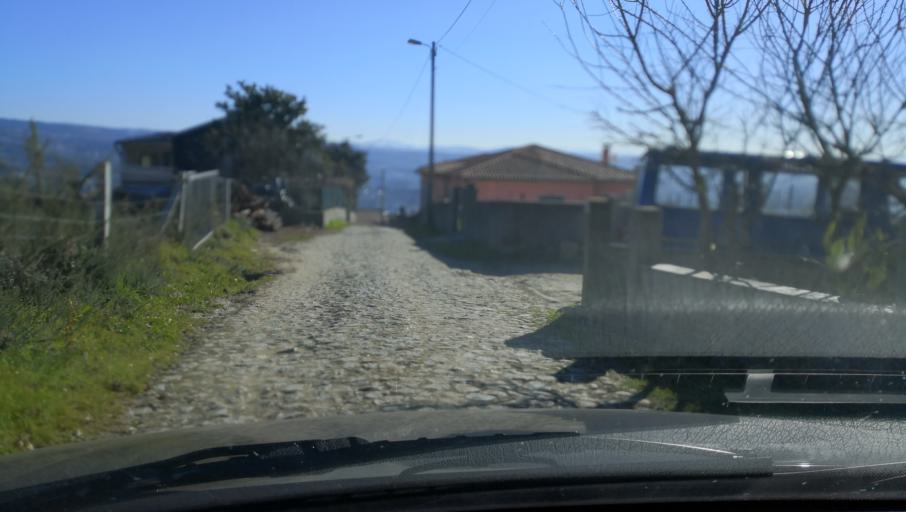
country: PT
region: Vila Real
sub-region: Vila Real
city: Vila Real
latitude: 41.3314
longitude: -7.7563
